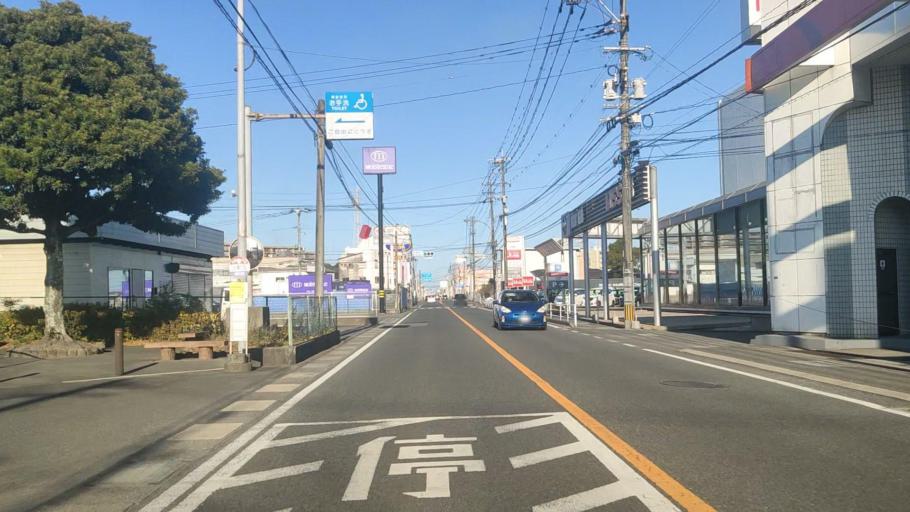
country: JP
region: Oita
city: Oita
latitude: 33.2146
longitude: 131.6109
